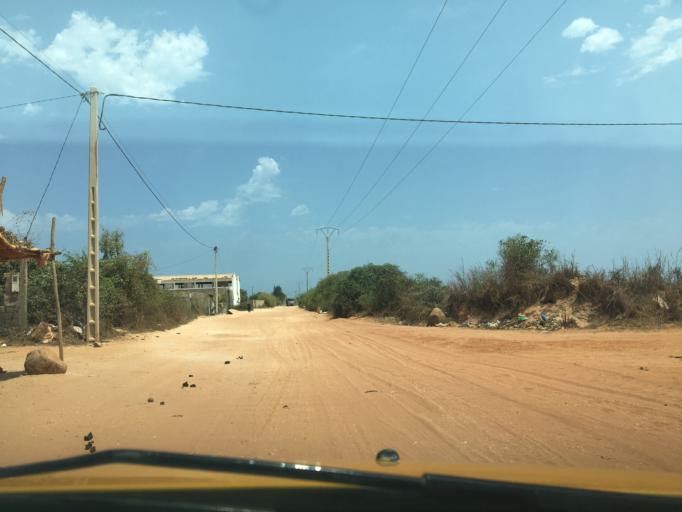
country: SN
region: Thies
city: Thies
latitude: 14.8120
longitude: -17.1920
